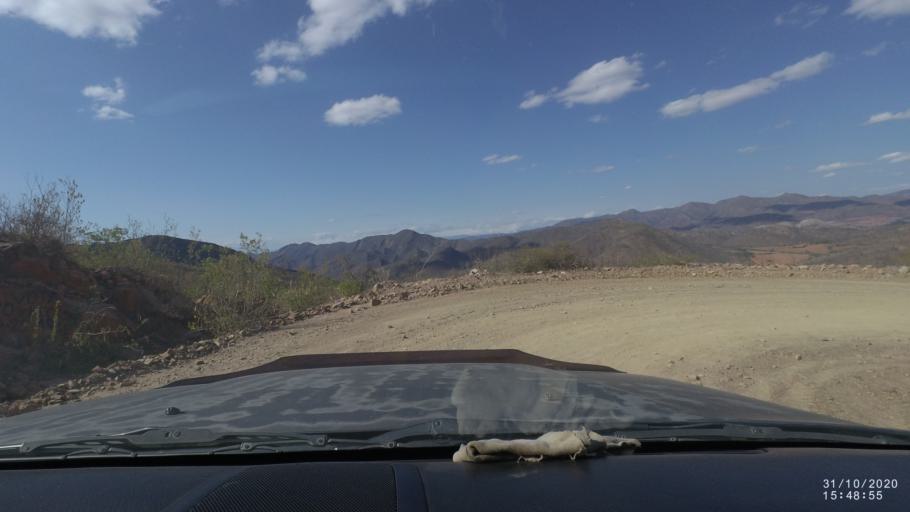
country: BO
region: Chuquisaca
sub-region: Provincia Zudanez
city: Mojocoya
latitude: -18.3095
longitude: -64.7102
